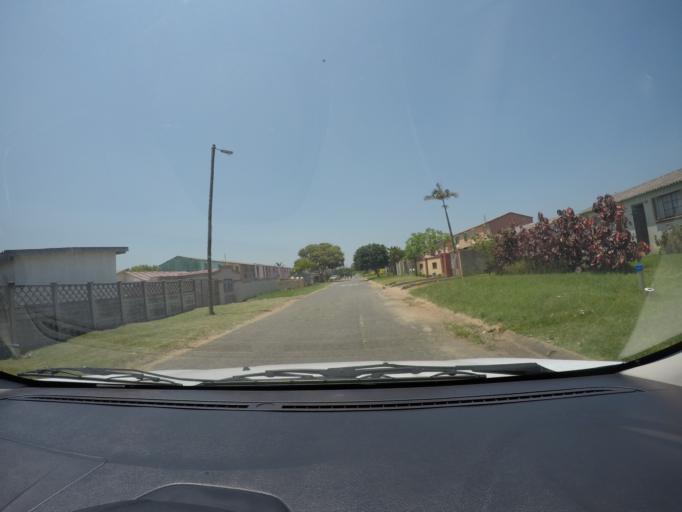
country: ZA
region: KwaZulu-Natal
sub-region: uThungulu District Municipality
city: eSikhawini
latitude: -28.8803
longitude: 31.8921
